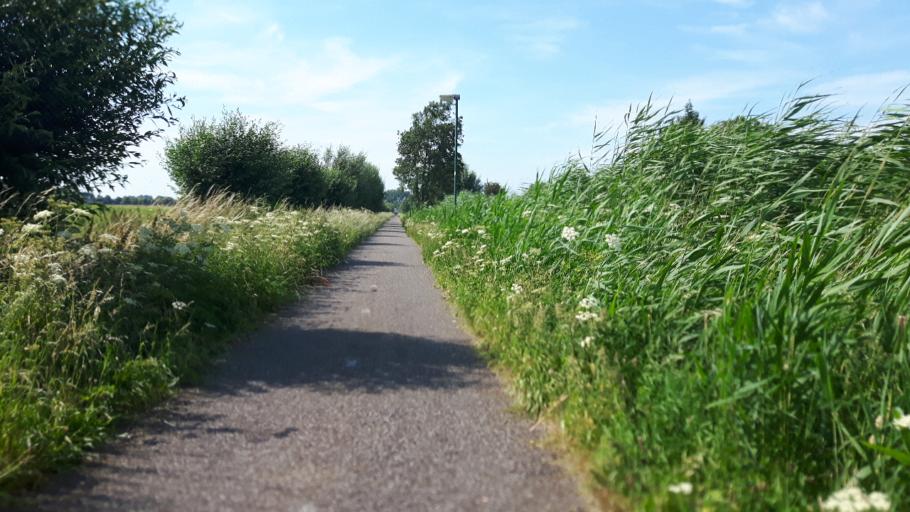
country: NL
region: Utrecht
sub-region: Gemeente Oudewater
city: Oudewater
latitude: 52.0103
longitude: 4.8851
